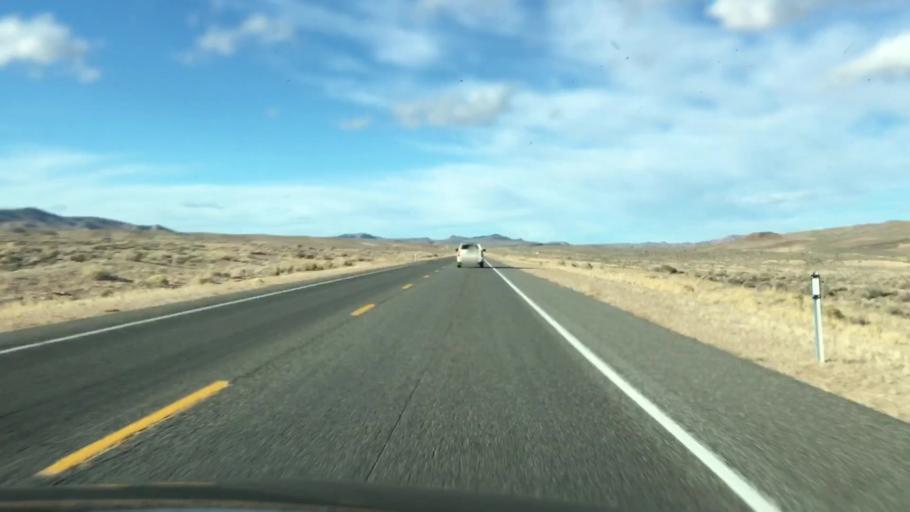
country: US
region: Nevada
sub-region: Esmeralda County
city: Goldfield
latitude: 37.5480
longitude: -117.1965
